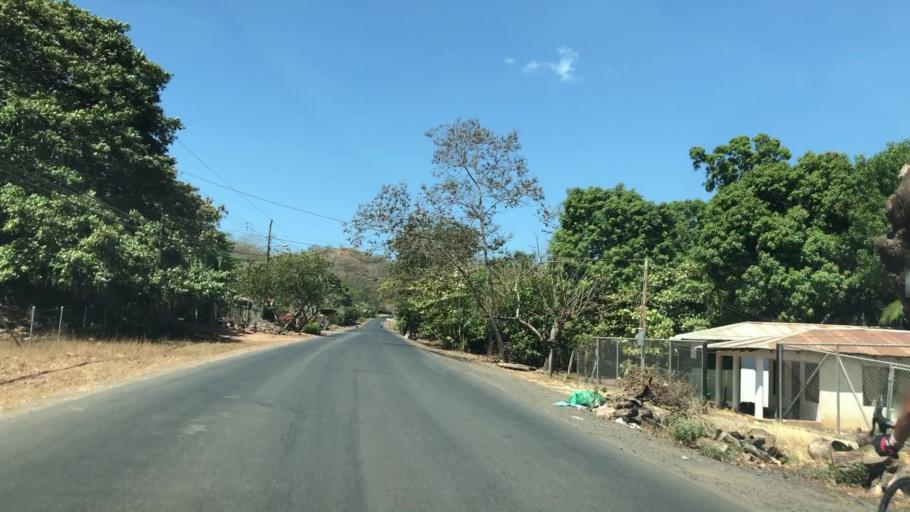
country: CR
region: Guanacaste
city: Belen
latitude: 10.3657
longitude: -85.7934
